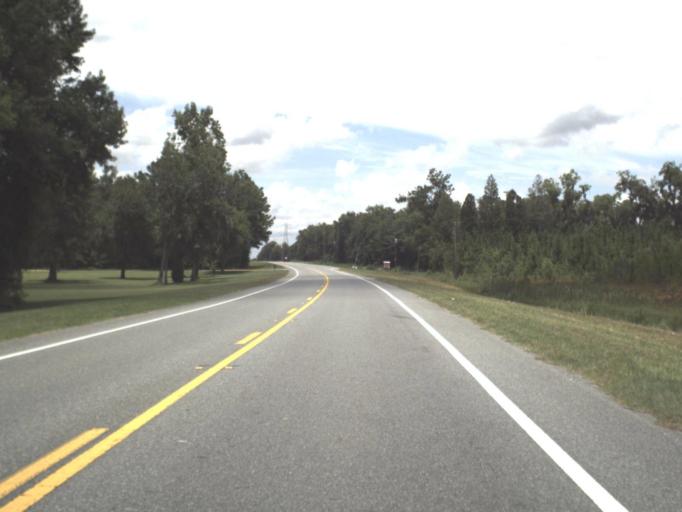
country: US
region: Florida
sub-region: Suwannee County
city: Live Oak
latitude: 30.3619
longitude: -82.9426
